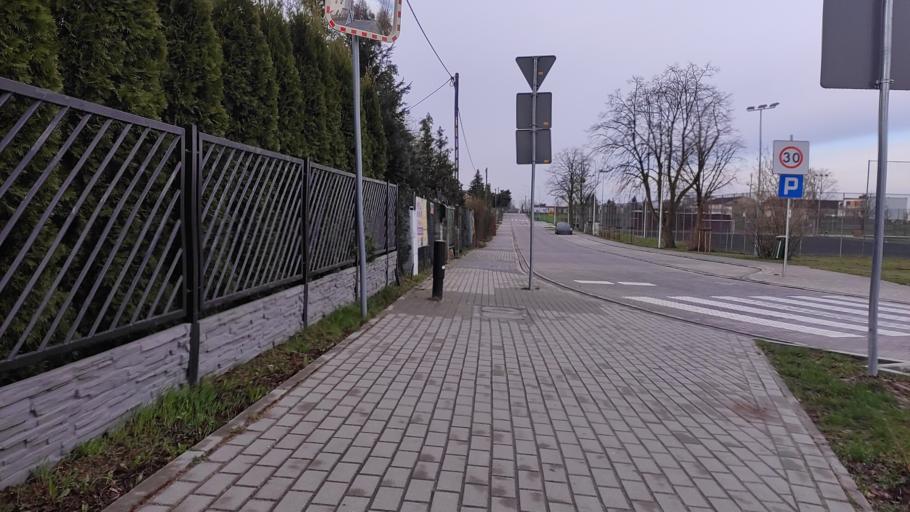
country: PL
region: Greater Poland Voivodeship
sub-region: Powiat poznanski
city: Kostrzyn
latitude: 52.4018
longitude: 17.1633
